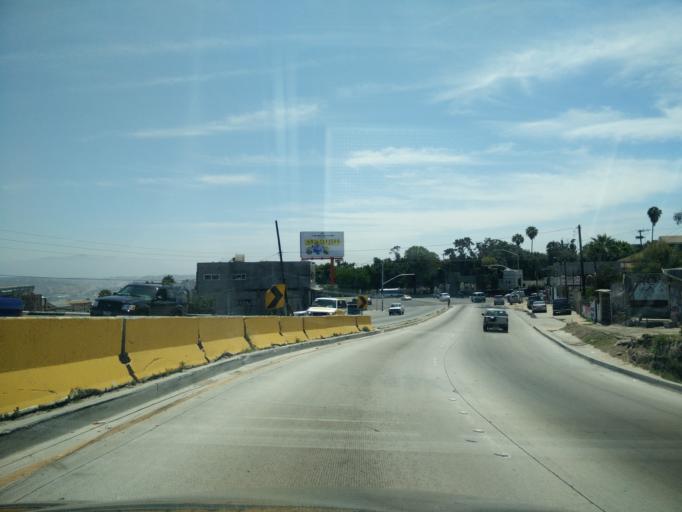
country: MX
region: Baja California
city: Tijuana
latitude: 32.5323
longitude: -117.0645
